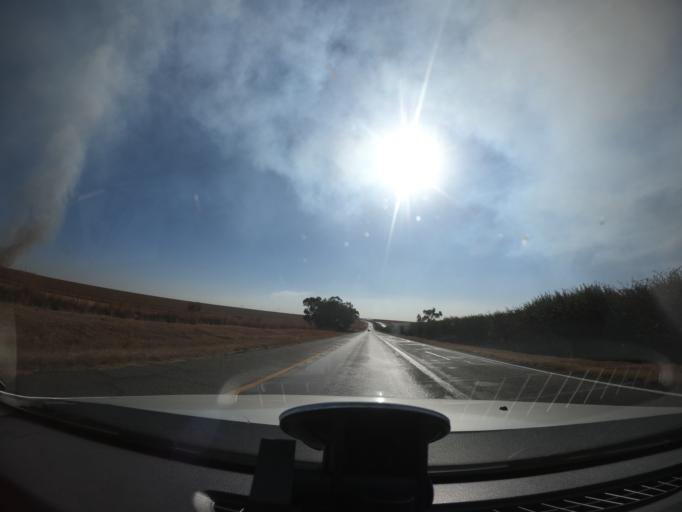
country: ZA
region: Gauteng
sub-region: Sedibeng District Municipality
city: Heidelberg
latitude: -26.4499
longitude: 28.3183
